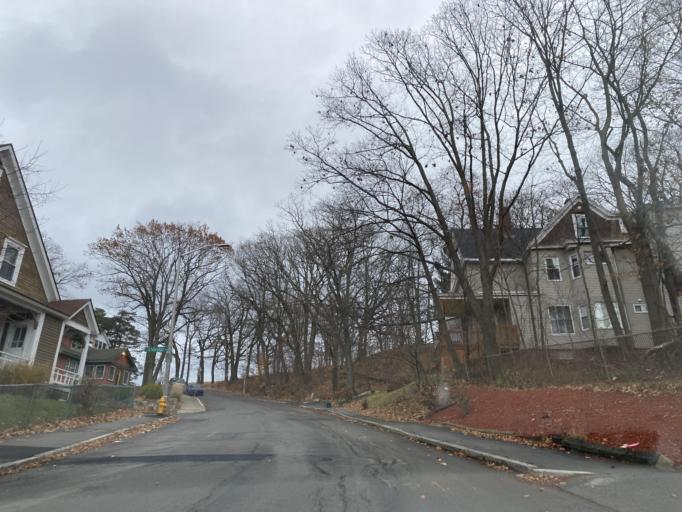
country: US
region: Massachusetts
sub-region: Worcester County
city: Worcester
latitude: 42.2805
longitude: -71.7901
